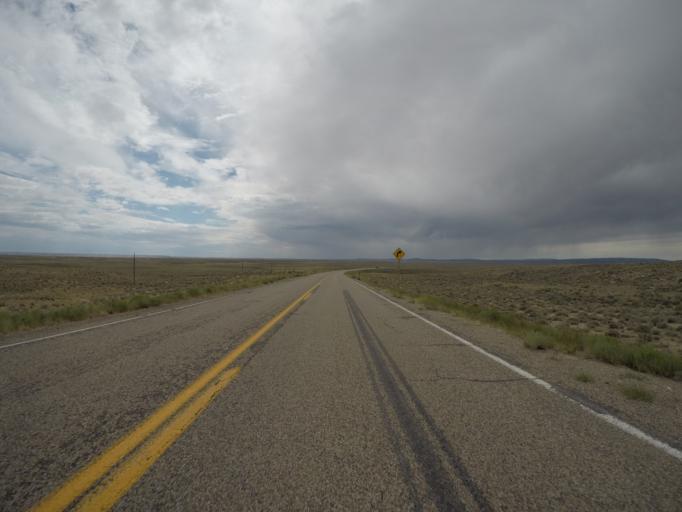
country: US
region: Wyoming
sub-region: Lincoln County
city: Kemmerer
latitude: 41.9641
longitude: -110.0975
